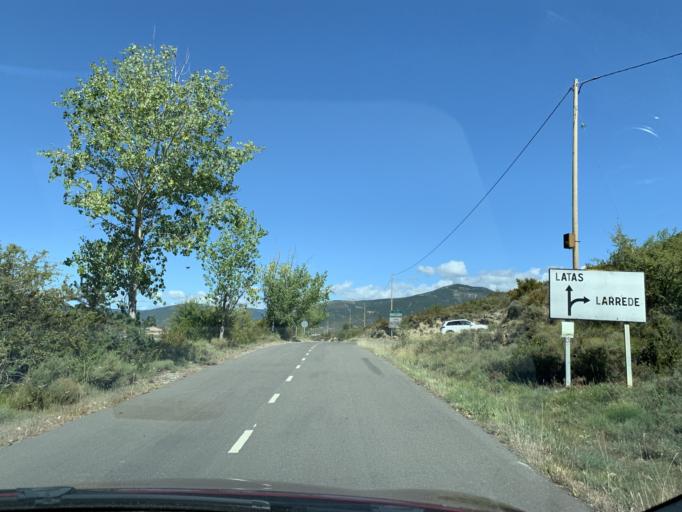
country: ES
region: Aragon
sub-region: Provincia de Huesca
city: Sabinanigo
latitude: 42.5215
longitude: -0.3279
